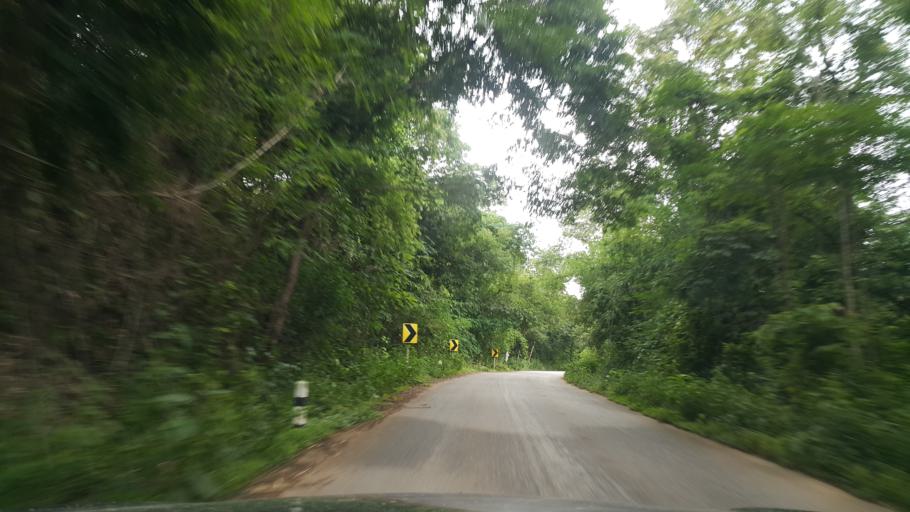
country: TH
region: Loei
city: Na Haeo
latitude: 17.4911
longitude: 100.8082
